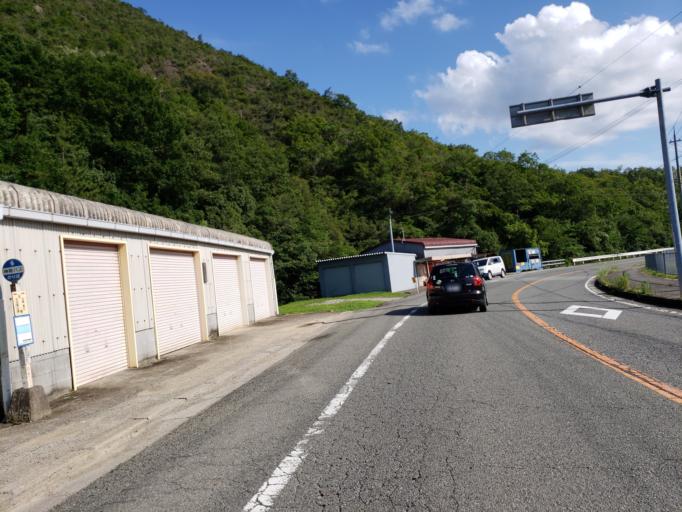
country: JP
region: Hyogo
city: Kakogawacho-honmachi
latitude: 34.8799
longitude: 134.7997
